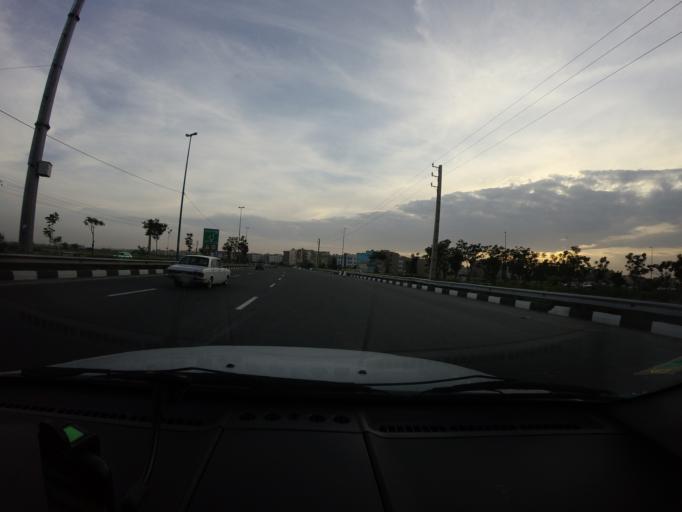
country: IR
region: Tehran
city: Eslamshahr
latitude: 35.5331
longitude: 51.2342
